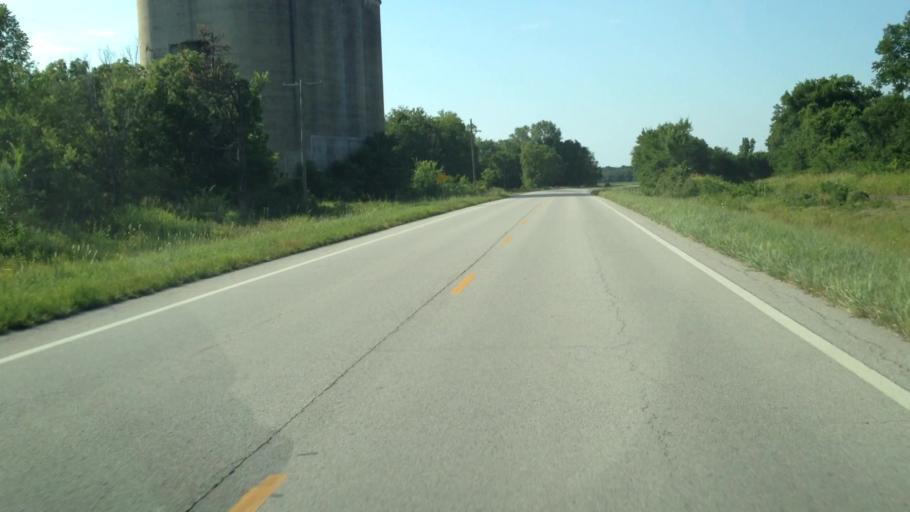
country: US
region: Kansas
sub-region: Allen County
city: Iola
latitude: 38.0275
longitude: -95.1729
